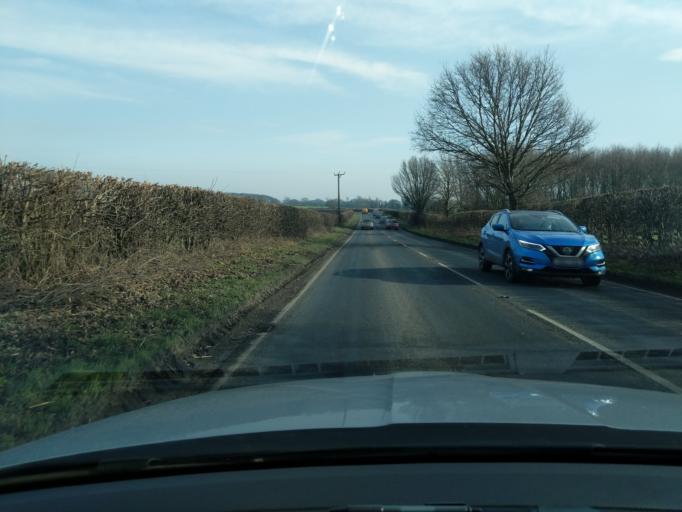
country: GB
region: England
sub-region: North Yorkshire
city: Bedale
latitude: 54.3107
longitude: -1.6558
